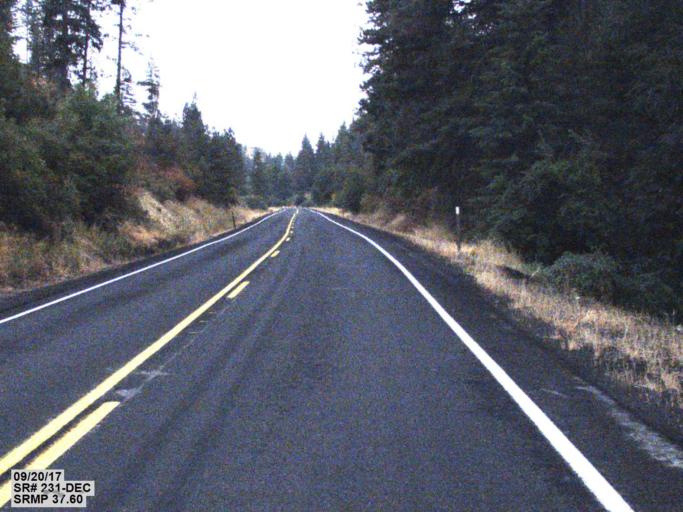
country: US
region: Washington
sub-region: Spokane County
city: Medical Lake
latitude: 47.7561
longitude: -117.8904
